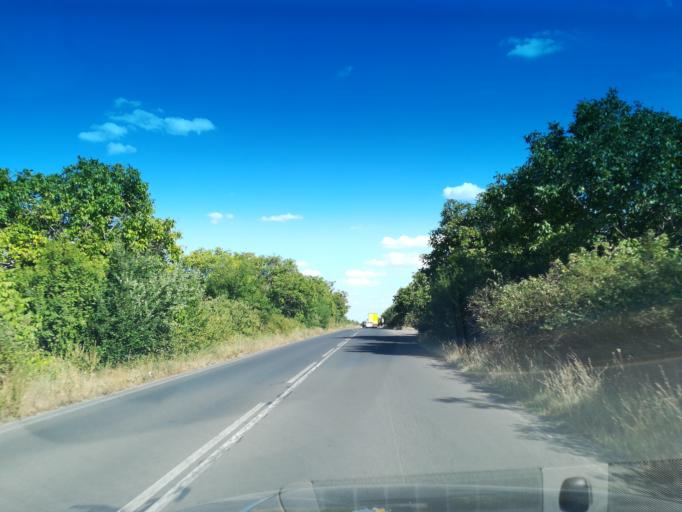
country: BG
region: Stara Zagora
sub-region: Obshtina Chirpan
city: Chirpan
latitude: 42.0602
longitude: 25.2450
